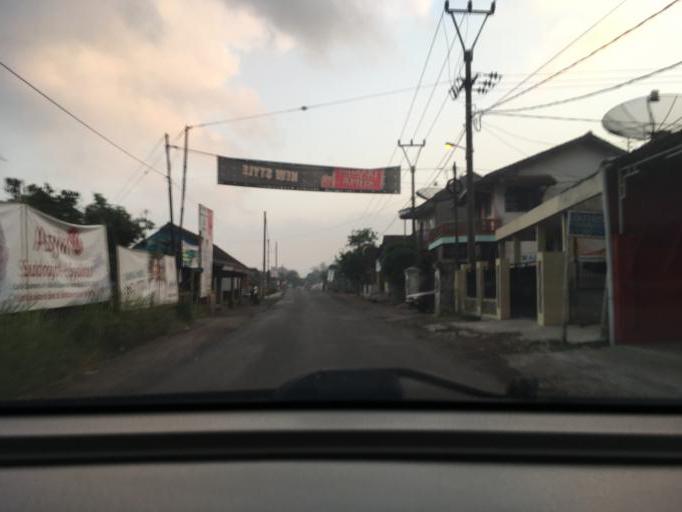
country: ID
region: West Java
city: Padamulya
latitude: -7.2050
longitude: 108.1996
